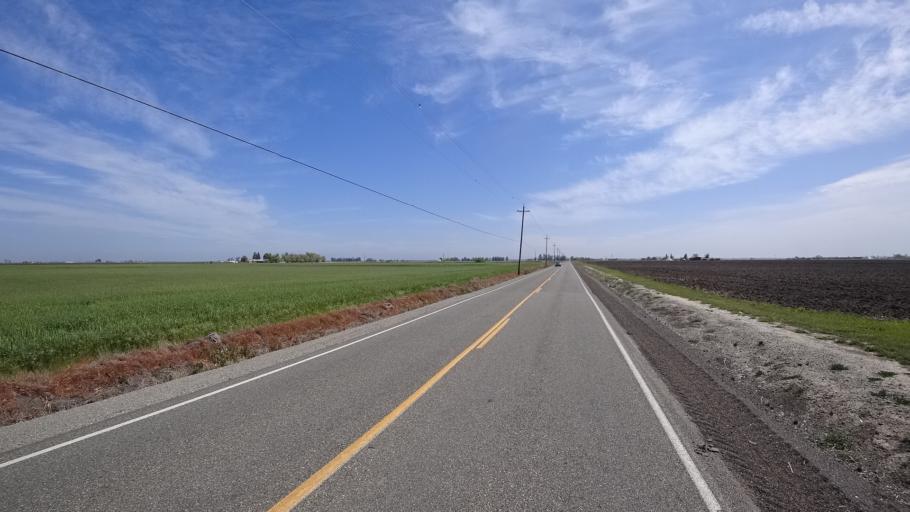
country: US
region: California
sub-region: Glenn County
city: Willows
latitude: 39.5828
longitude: -122.0837
